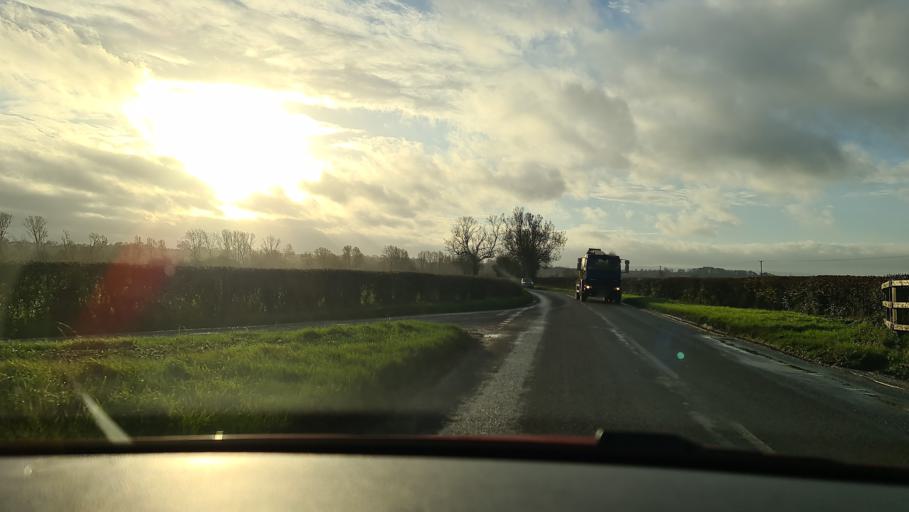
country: GB
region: England
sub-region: Buckinghamshire
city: Haddenham
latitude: 51.8001
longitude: -0.9494
